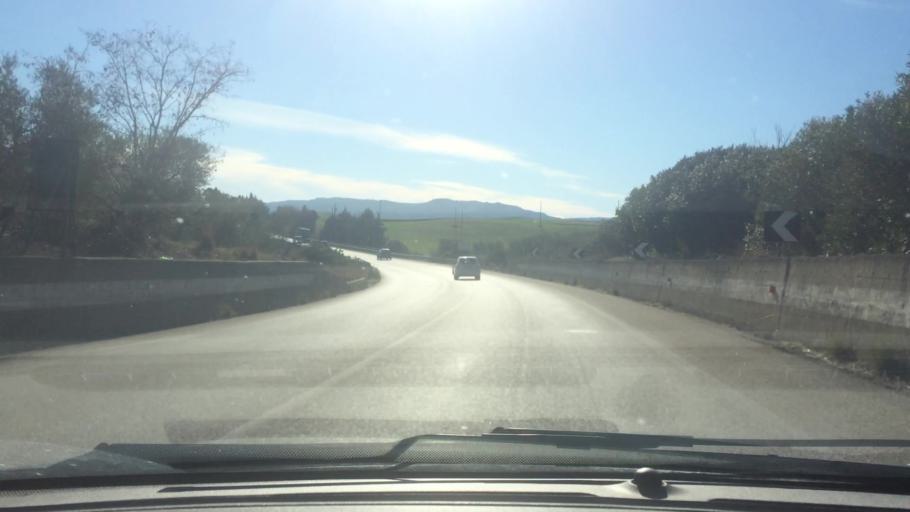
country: IT
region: Basilicate
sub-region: Provincia di Matera
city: Miglionico
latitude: 40.5927
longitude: 16.5734
